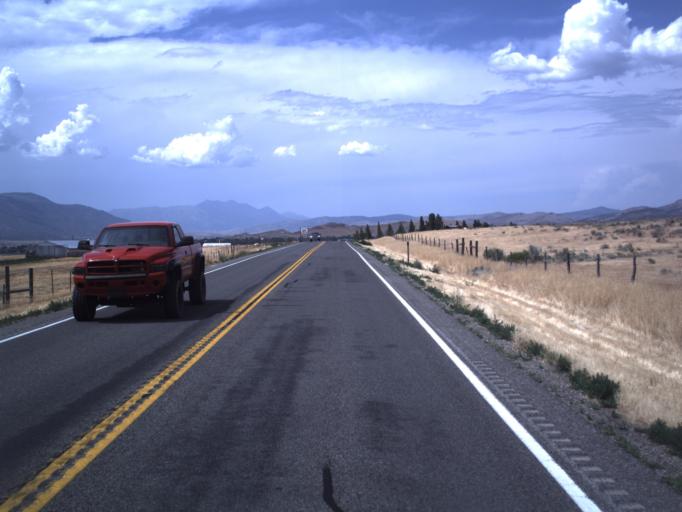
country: US
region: Utah
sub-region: Sanpete County
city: Moroni
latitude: 39.4978
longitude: -111.5646
